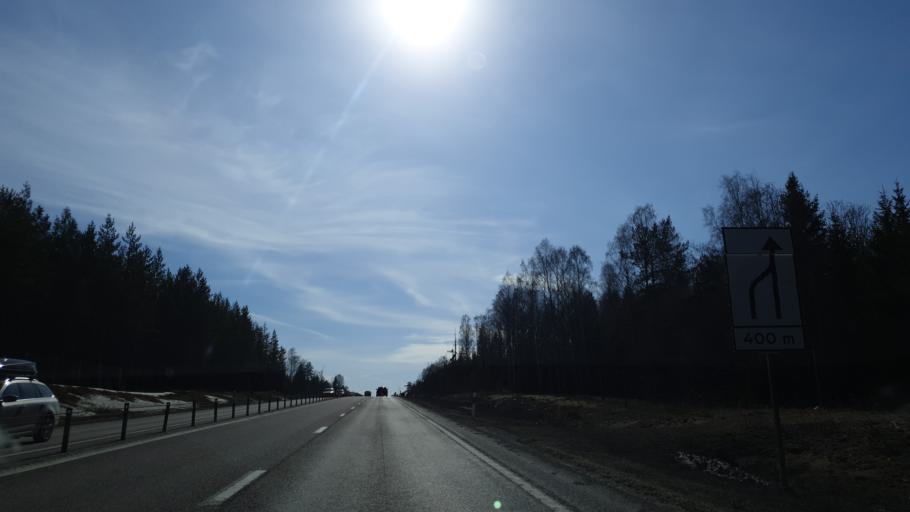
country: SE
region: Vaesternorrland
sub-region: Haernoesands Kommun
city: Haernoesand
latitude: 62.5716
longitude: 17.7433
